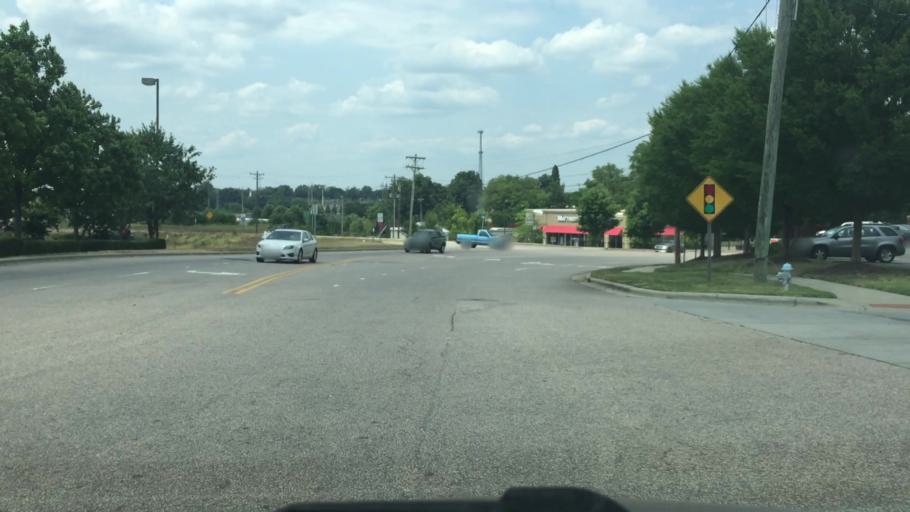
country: US
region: North Carolina
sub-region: Rowan County
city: Salisbury
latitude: 35.6535
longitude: -80.4582
